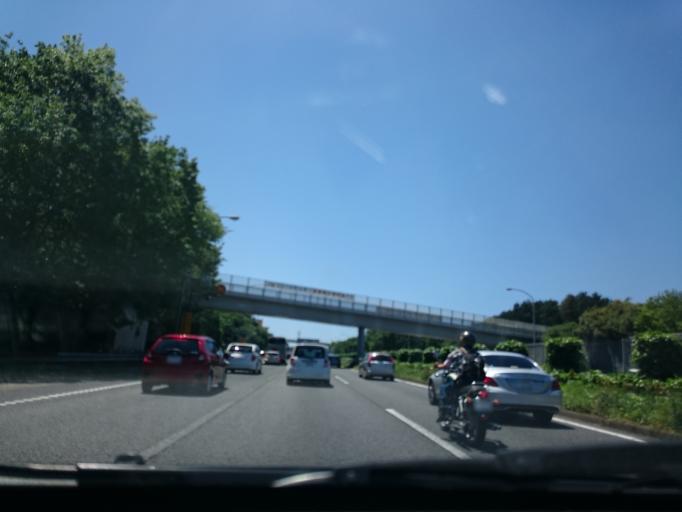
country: JP
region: Kanagawa
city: Minami-rinkan
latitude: 35.5101
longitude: 139.4858
